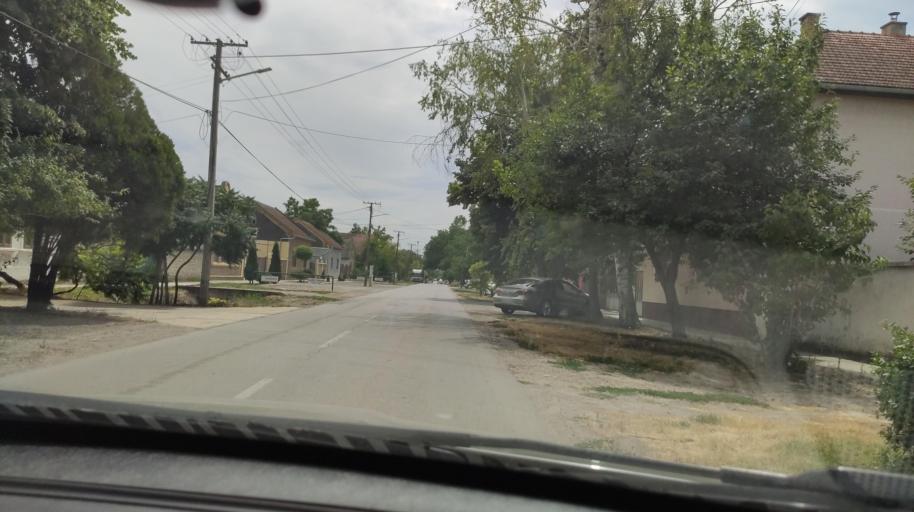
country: RS
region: Autonomna Pokrajina Vojvodina
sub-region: Juznobacki Okrug
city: Temerin
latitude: 45.4102
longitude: 19.8831
